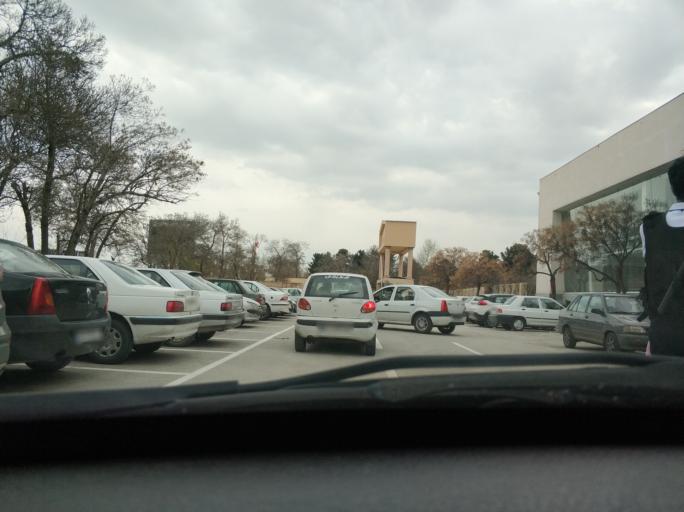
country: IR
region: Razavi Khorasan
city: Mashhad
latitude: 36.2557
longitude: 59.6103
